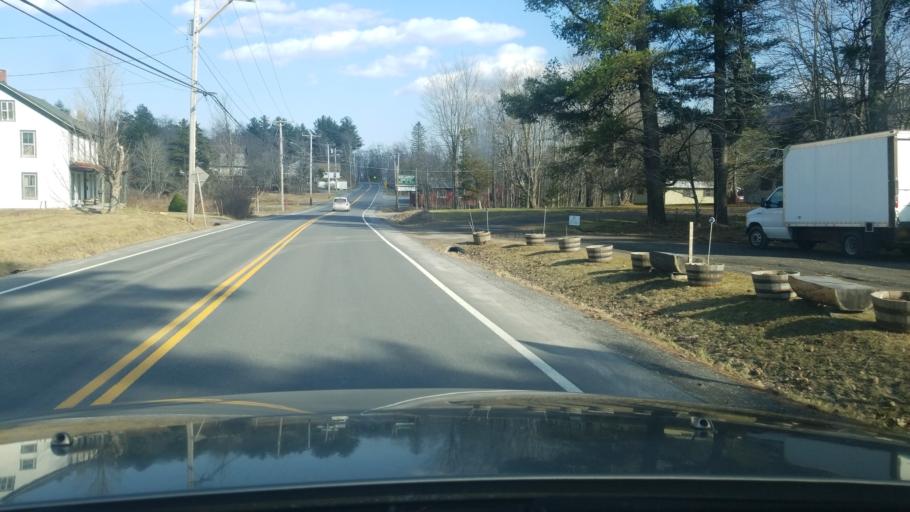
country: US
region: New York
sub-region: Ulster County
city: Manorville
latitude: 42.1965
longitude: -74.1070
